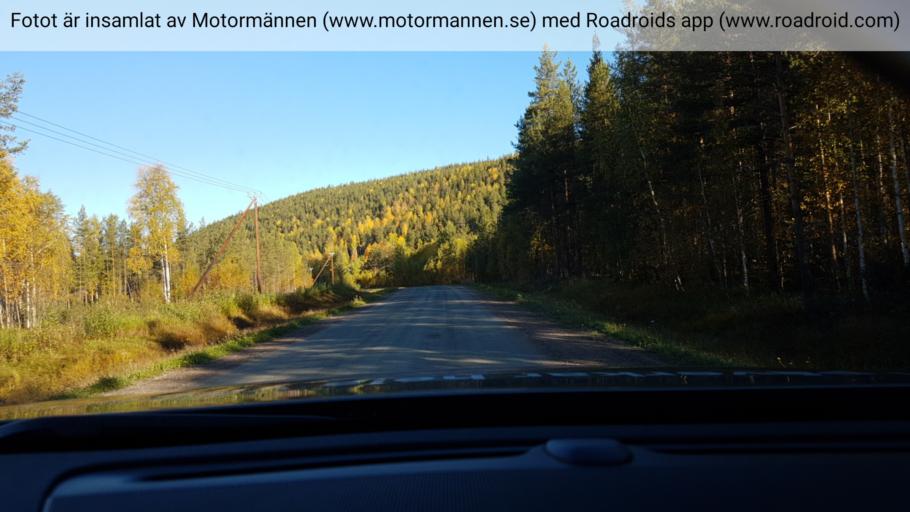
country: SE
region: Norrbotten
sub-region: Alvsbyns Kommun
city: AElvsbyn
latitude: 66.1727
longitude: 21.2427
